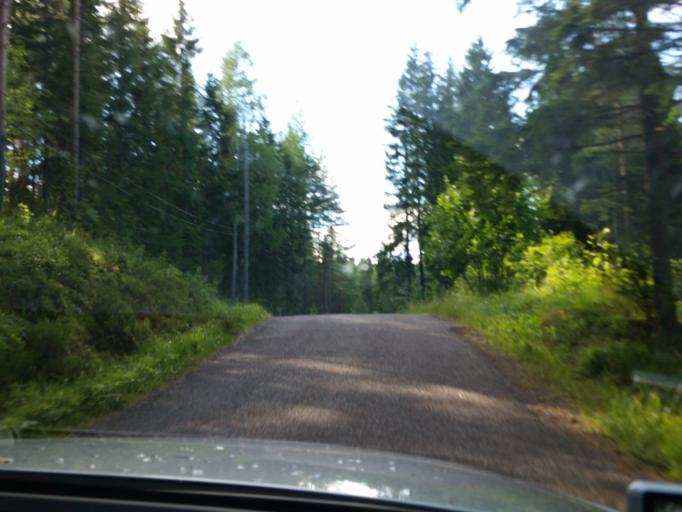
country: FI
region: Uusimaa
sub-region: Helsinki
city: Kaerkoelae
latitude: 60.5545
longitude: 23.9904
